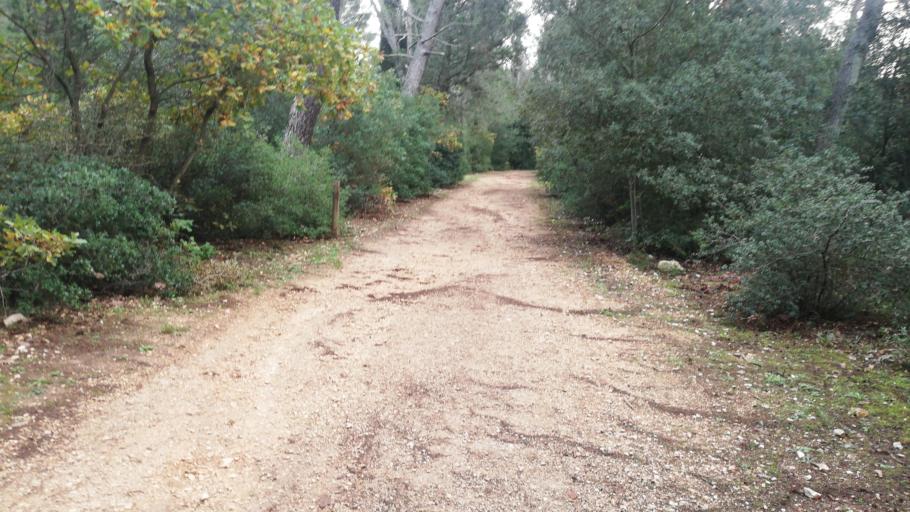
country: IT
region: Apulia
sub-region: Provincia di Bari
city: Cassano delle Murge
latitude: 40.8797
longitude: 16.7120
